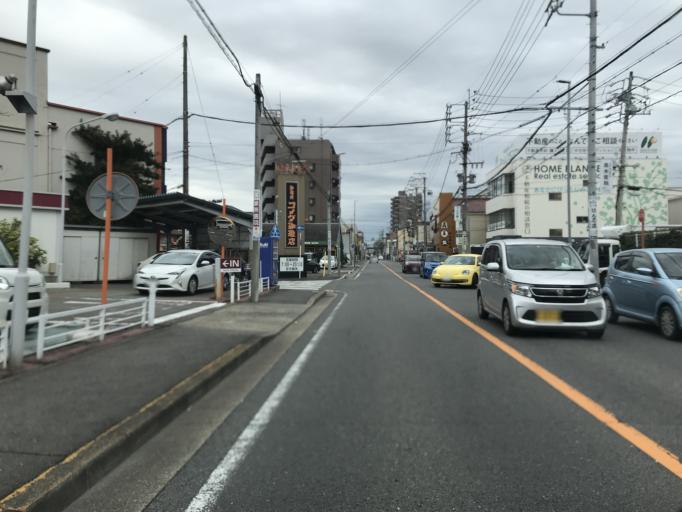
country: JP
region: Aichi
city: Nagoya-shi
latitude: 35.1915
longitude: 136.8791
